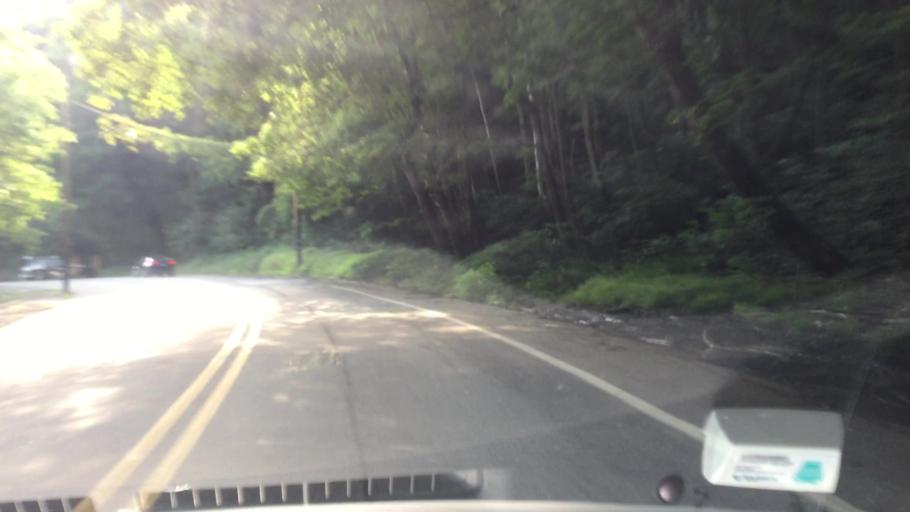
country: US
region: Pennsylvania
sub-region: Allegheny County
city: Mount Oliver
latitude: 40.4118
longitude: -80.0000
